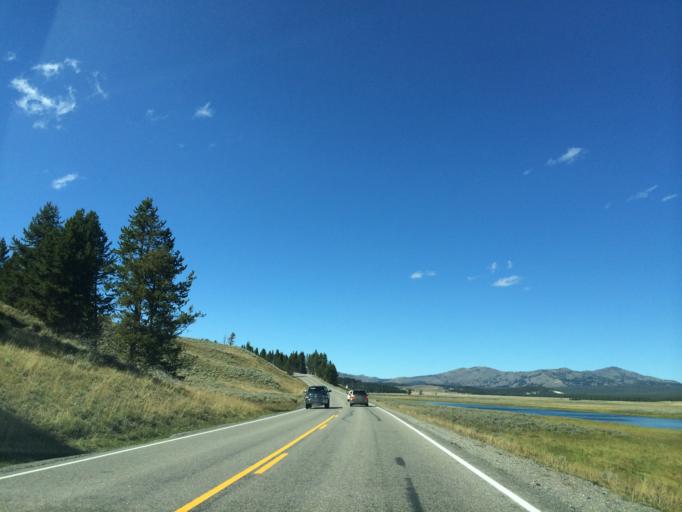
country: US
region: Montana
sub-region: Gallatin County
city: West Yellowstone
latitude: 44.6639
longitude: -110.4650
